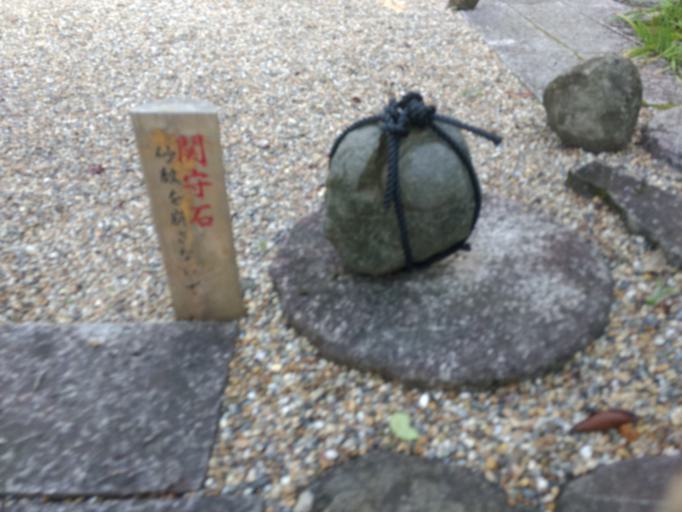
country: JP
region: Nara
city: Sakurai
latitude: 34.5366
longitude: 135.8552
